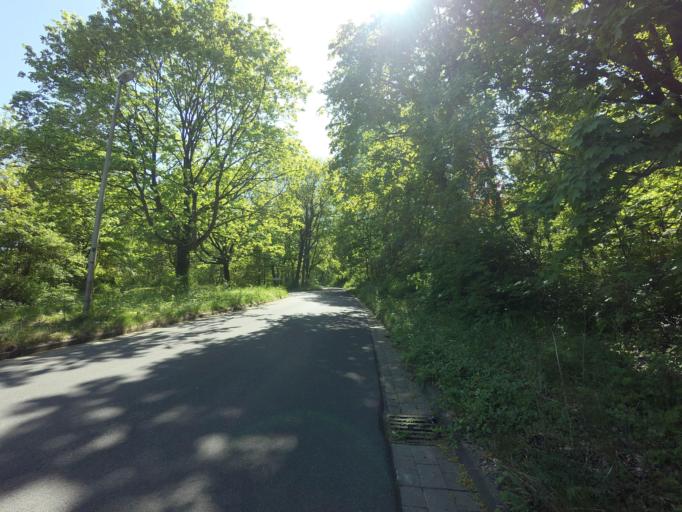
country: DE
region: Lower Saxony
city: Hildesheim
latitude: 52.1458
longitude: 9.9732
